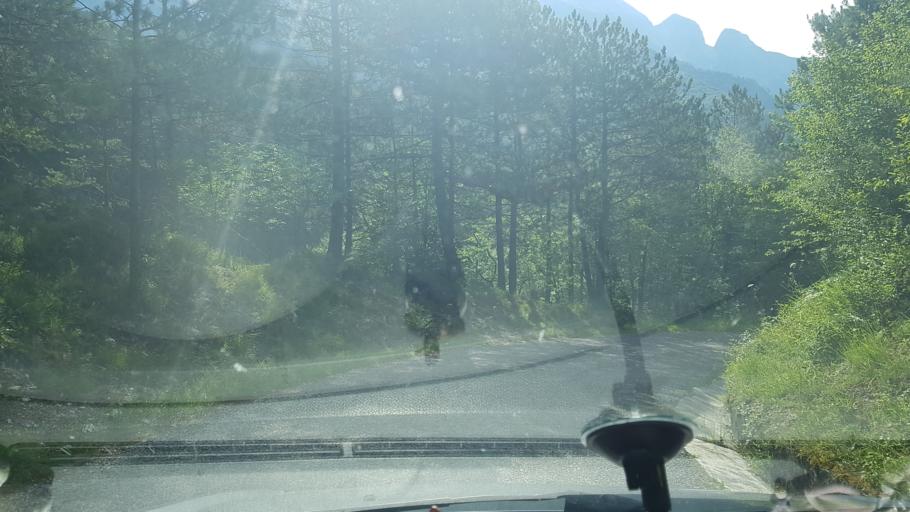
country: IT
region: Friuli Venezia Giulia
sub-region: Provincia di Udine
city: Prato
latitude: 46.3528
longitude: 13.3830
